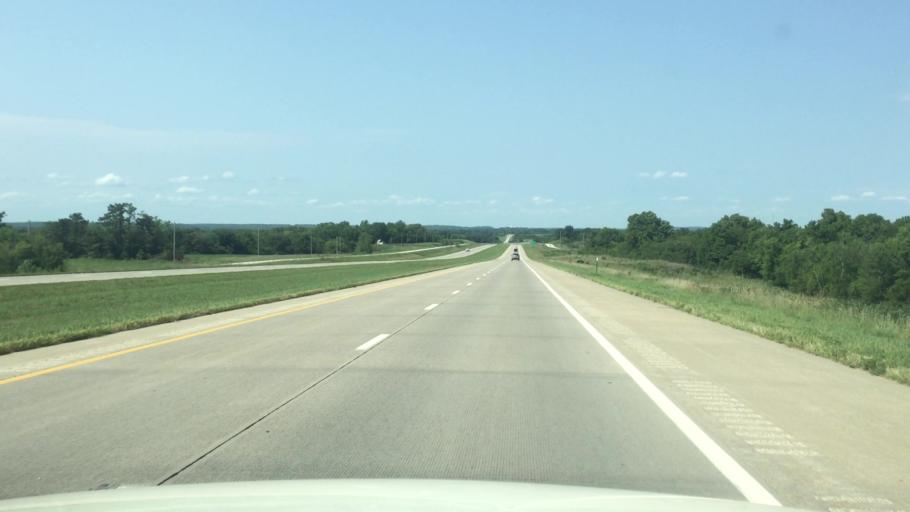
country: US
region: Kansas
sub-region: Linn County
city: Pleasanton
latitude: 38.1178
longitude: -94.7133
